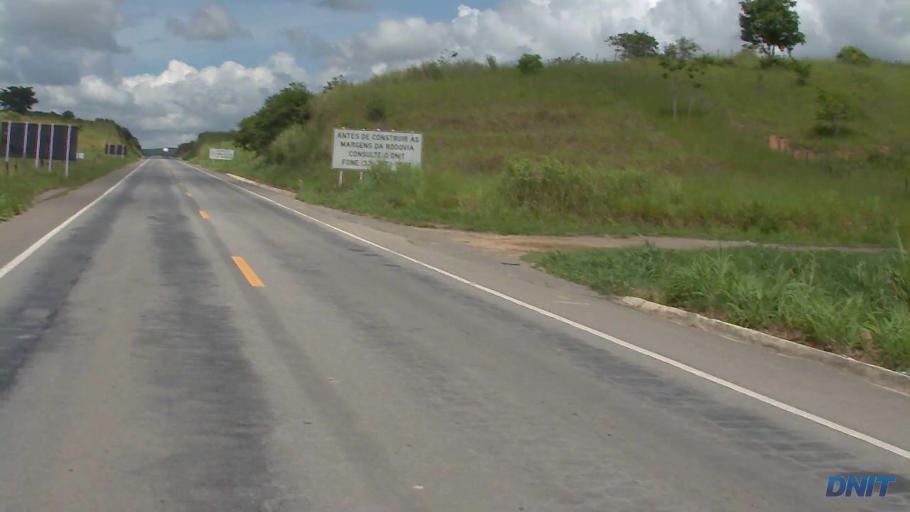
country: BR
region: Minas Gerais
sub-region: Governador Valadares
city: Governador Valadares
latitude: -18.9956
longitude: -42.1200
